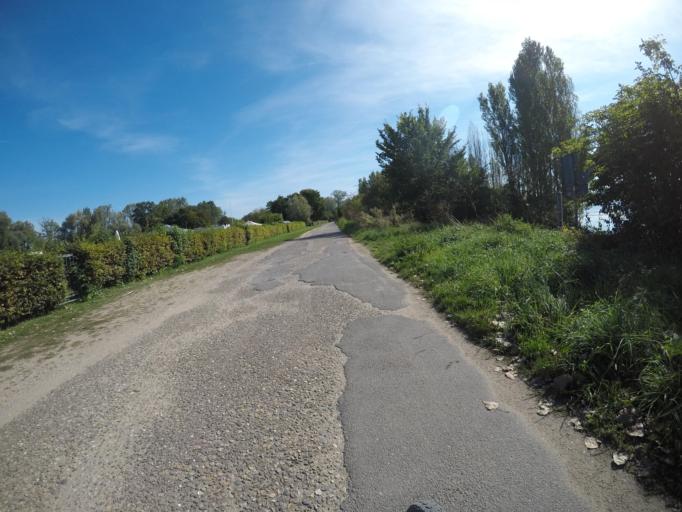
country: DE
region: Hesse
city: Biebesheim
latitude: 49.7678
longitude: 8.4356
